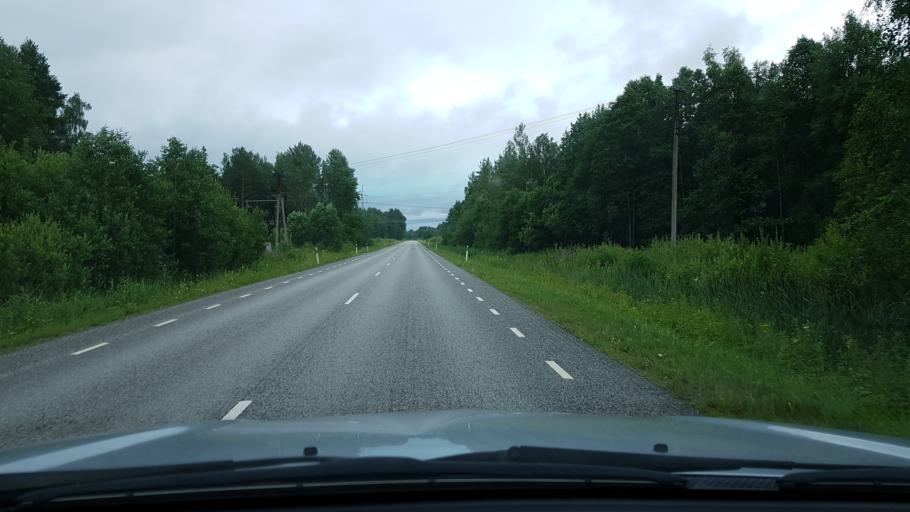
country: EE
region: Ida-Virumaa
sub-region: Narva-Joesuu linn
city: Narva-Joesuu
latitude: 59.3533
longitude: 27.9285
